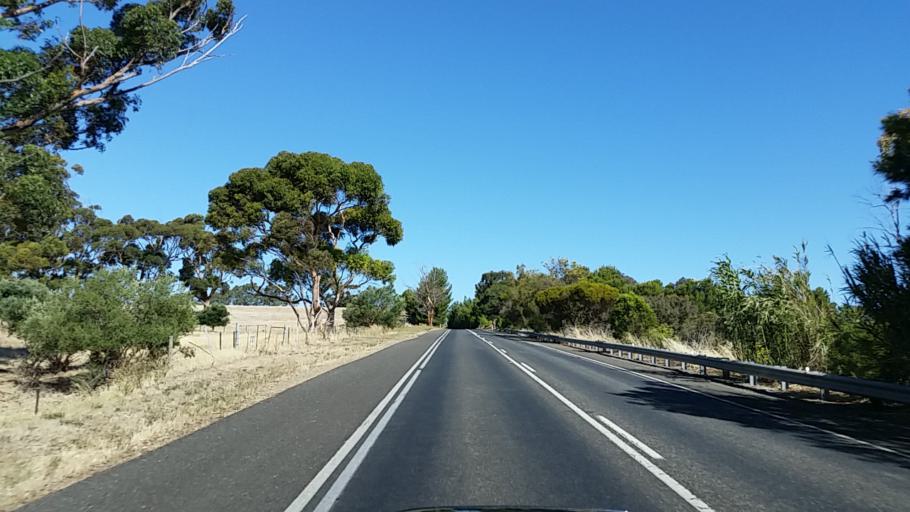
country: AU
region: South Australia
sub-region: Playford
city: One Tree Hill
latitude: -34.7140
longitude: 138.7369
